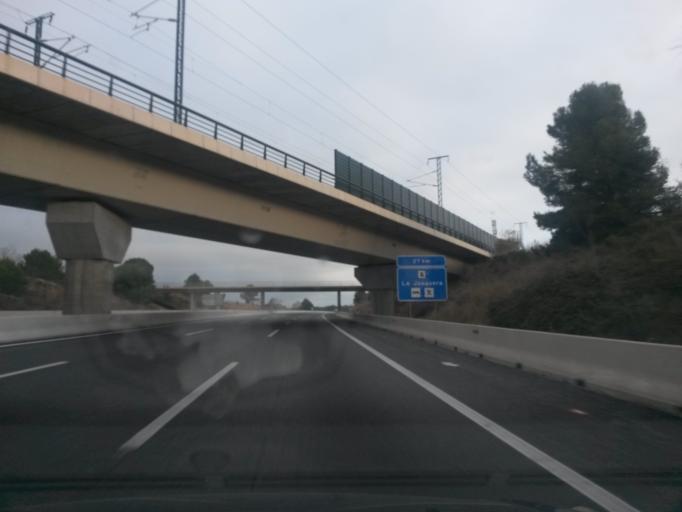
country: ES
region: Catalonia
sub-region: Provincia de Girona
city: Pontos
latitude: 42.1888
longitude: 2.9327
